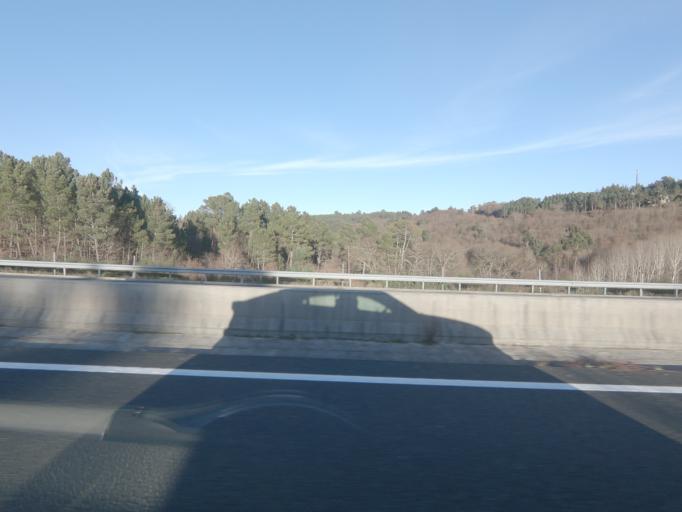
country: ES
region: Galicia
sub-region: Provincia de Ourense
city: Pinor
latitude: 42.4962
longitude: -8.0279
